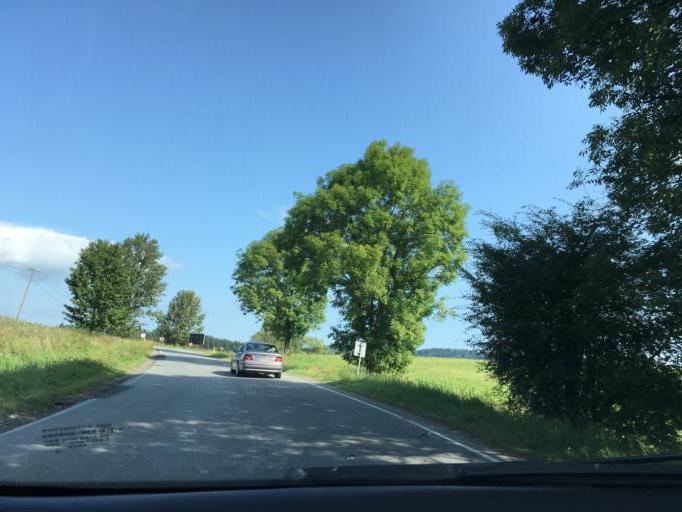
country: PL
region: Subcarpathian Voivodeship
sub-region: Powiat bieszczadzki
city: Czarna
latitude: 49.3289
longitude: 22.6710
